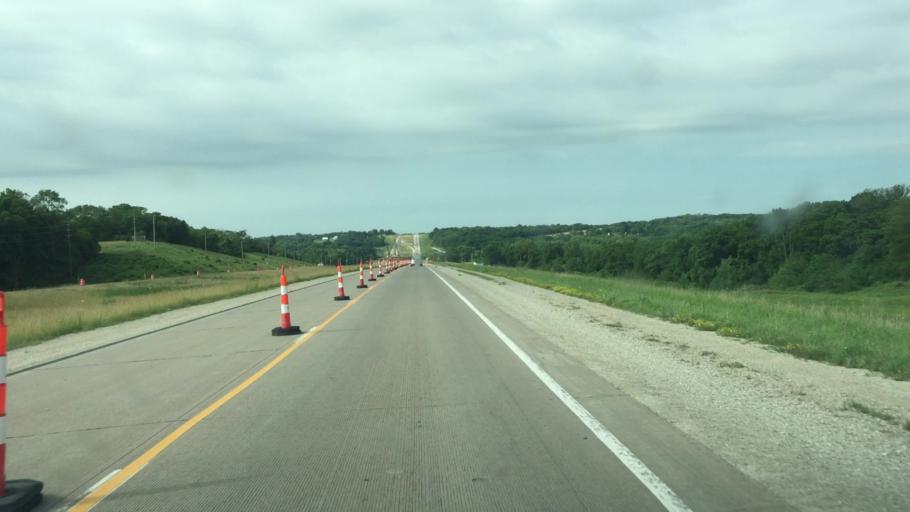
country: US
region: Iowa
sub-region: Henry County
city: Mount Pleasant
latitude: 40.9086
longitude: -91.5490
